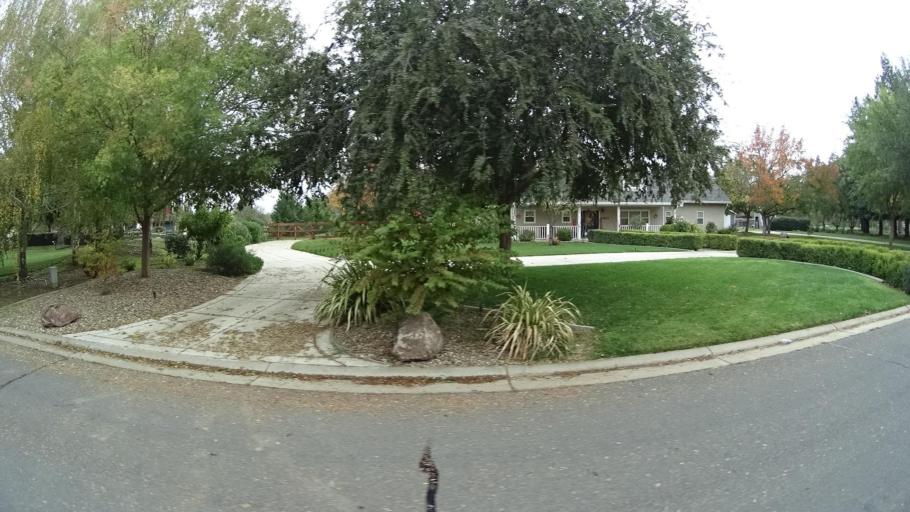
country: US
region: California
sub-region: Sacramento County
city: Wilton
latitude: 38.4424
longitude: -121.2933
